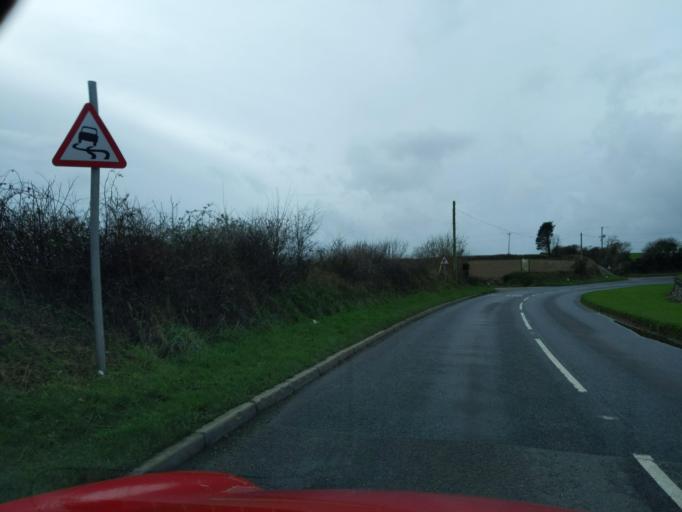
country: GB
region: England
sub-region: Cornwall
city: Duloe
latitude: 50.3566
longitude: -4.5158
